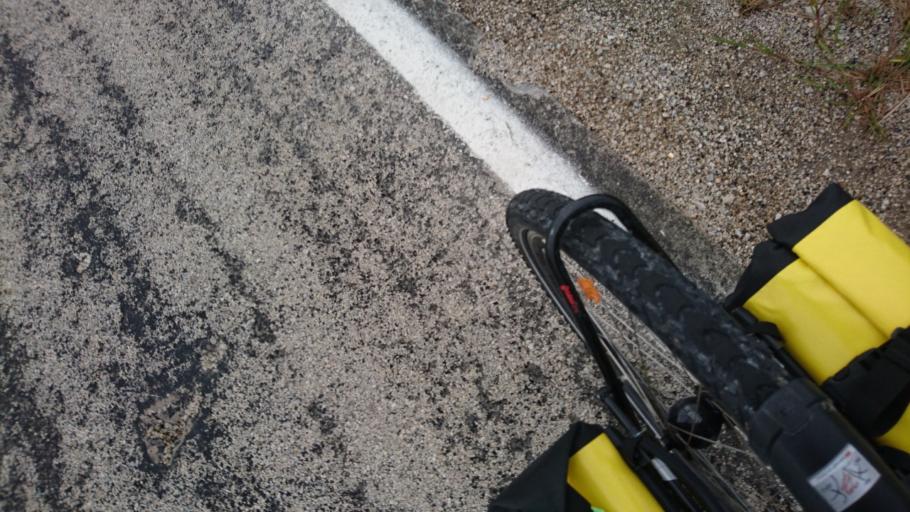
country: US
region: Illinois
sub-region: Montgomery County
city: Raymond
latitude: 39.3027
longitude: -89.6428
